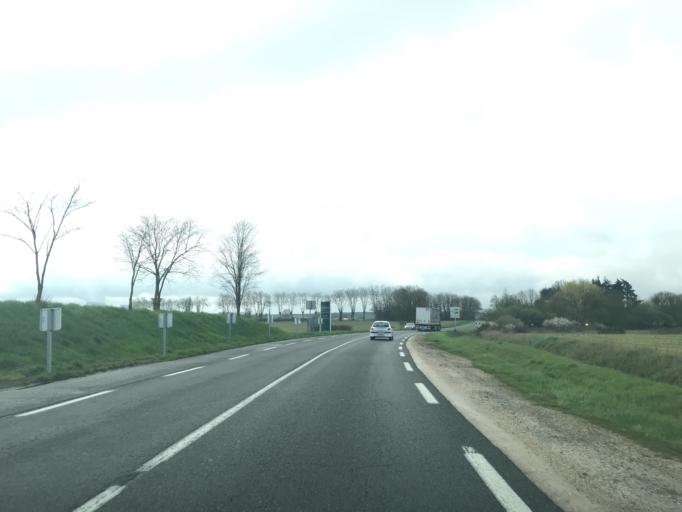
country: FR
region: Centre
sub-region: Departement du Loiret
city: Nevoy
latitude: 47.7154
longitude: 2.5870
